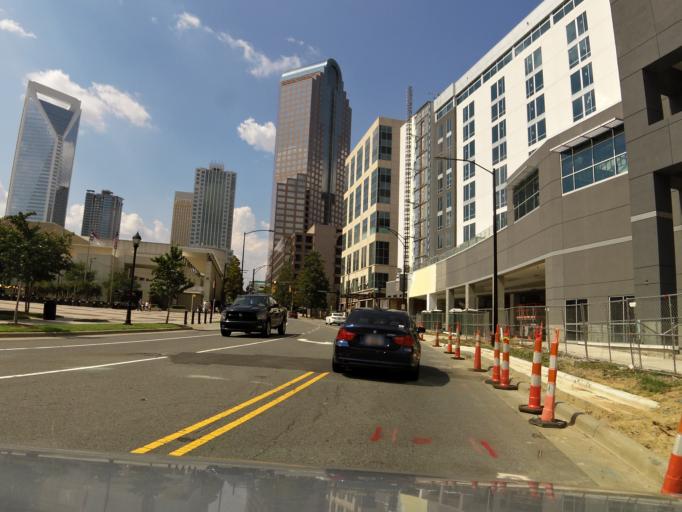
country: US
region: North Carolina
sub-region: Mecklenburg County
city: Charlotte
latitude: 35.2214
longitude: -80.8428
